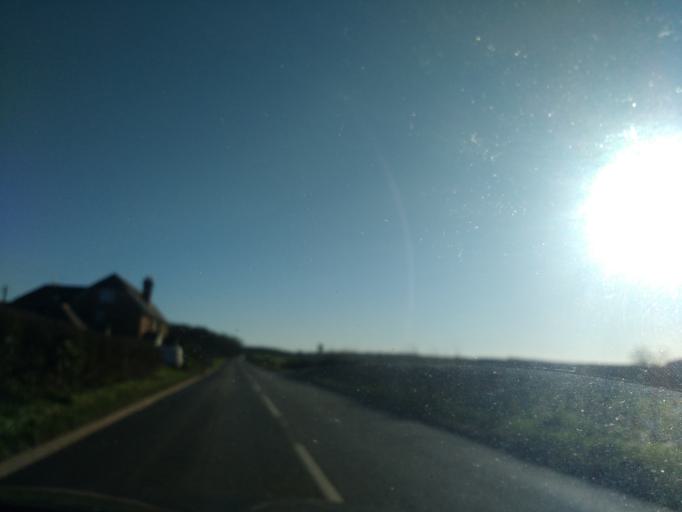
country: GB
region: England
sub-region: Isle of Wight
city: Newport
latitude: 50.7059
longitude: -1.2440
